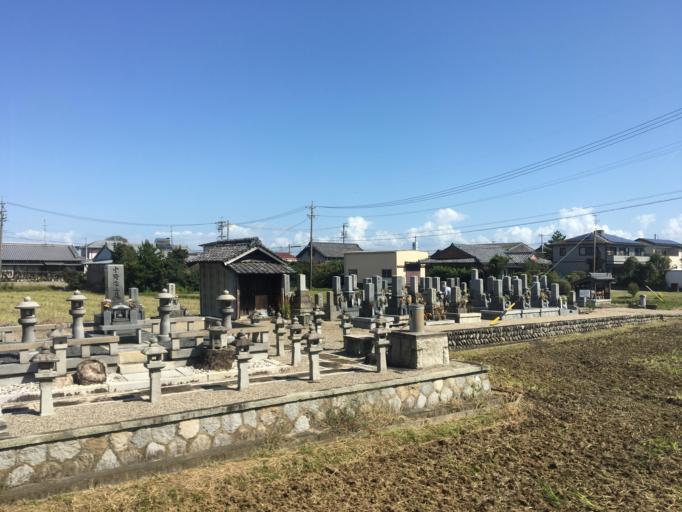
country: JP
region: Mie
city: Suzuka
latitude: 34.8735
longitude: 136.5945
